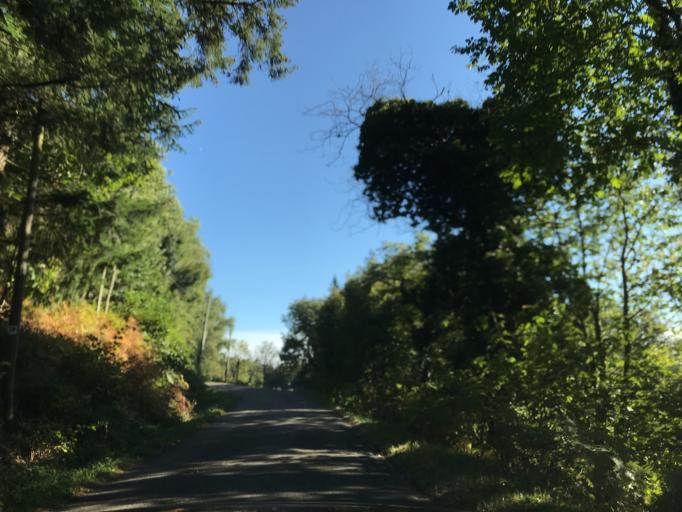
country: FR
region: Auvergne
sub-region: Departement du Puy-de-Dome
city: Escoutoux
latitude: 45.7698
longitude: 3.6195
